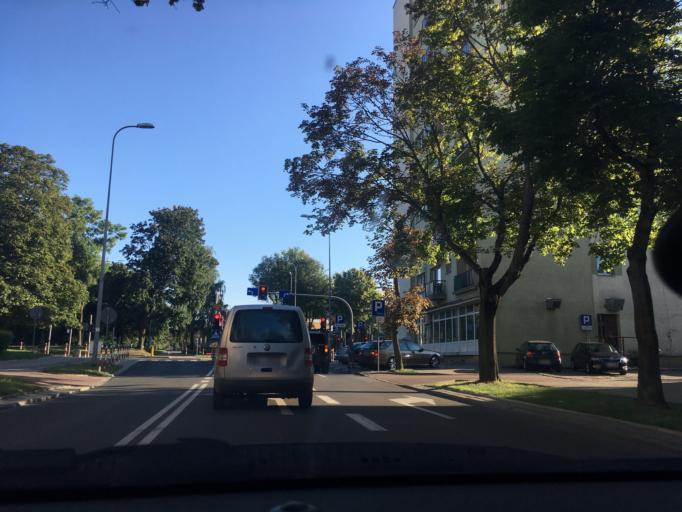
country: PL
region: Podlasie
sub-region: Bialystok
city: Bialystok
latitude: 53.1320
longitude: 23.1510
